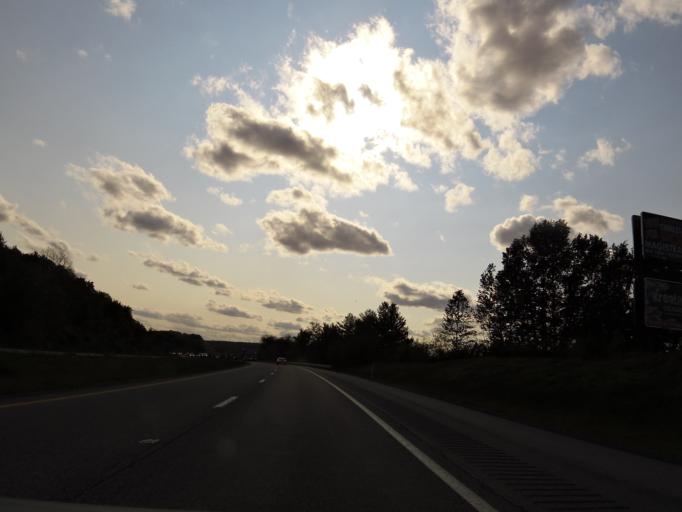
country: US
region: West Virginia
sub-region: Mercer County
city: Princeton
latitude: 37.3628
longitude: -81.0720
